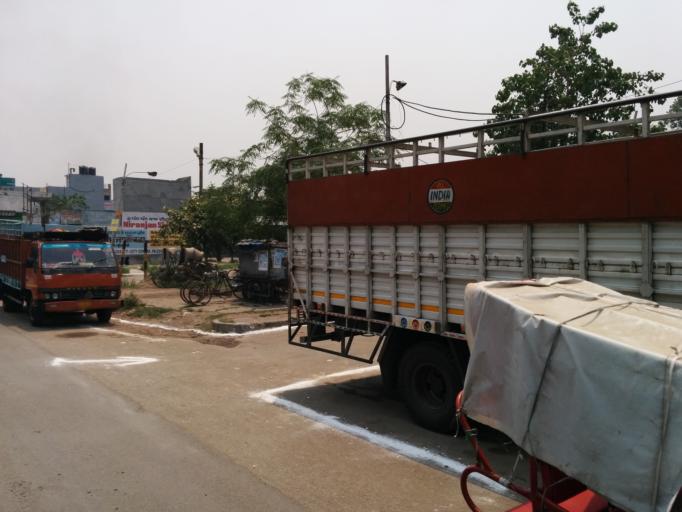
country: IN
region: Punjab
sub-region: Amritsar
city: Amritsar
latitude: 31.6284
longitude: 74.8863
